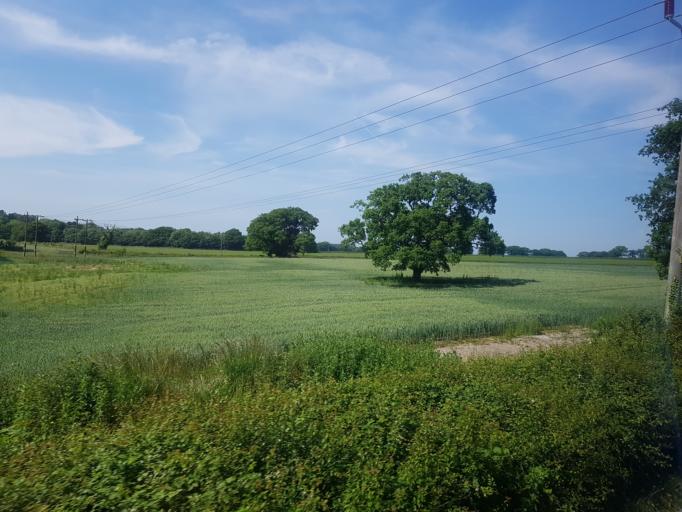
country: GB
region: England
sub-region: Isle of Wight
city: Newport
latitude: 50.7119
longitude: -1.2535
